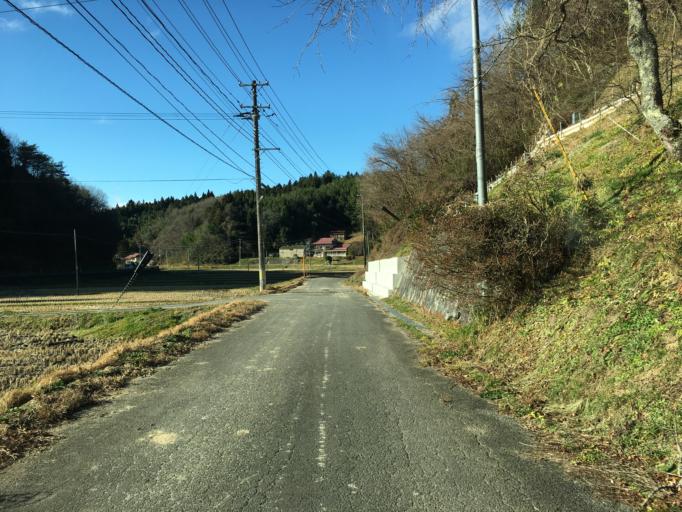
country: JP
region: Fukushima
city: Ishikawa
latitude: 37.2204
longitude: 140.5916
